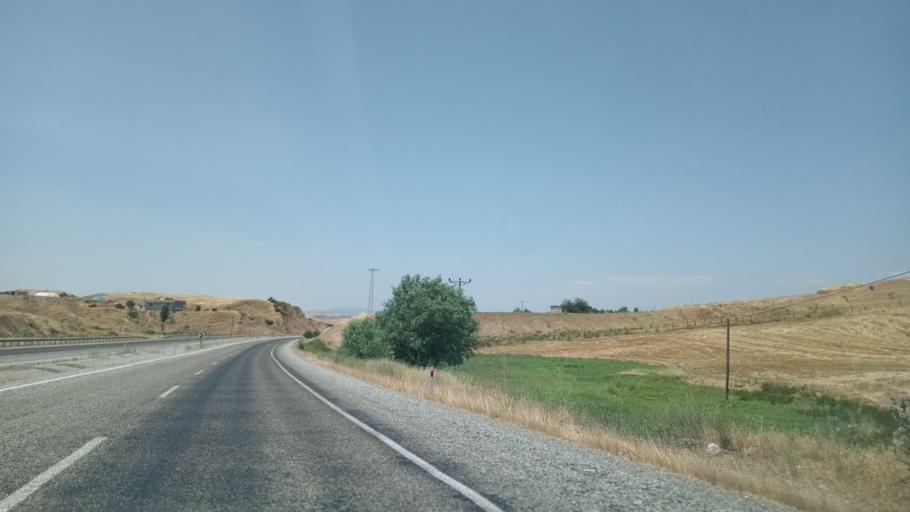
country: TR
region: Batman
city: Bekirhan
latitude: 38.1548
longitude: 41.3578
